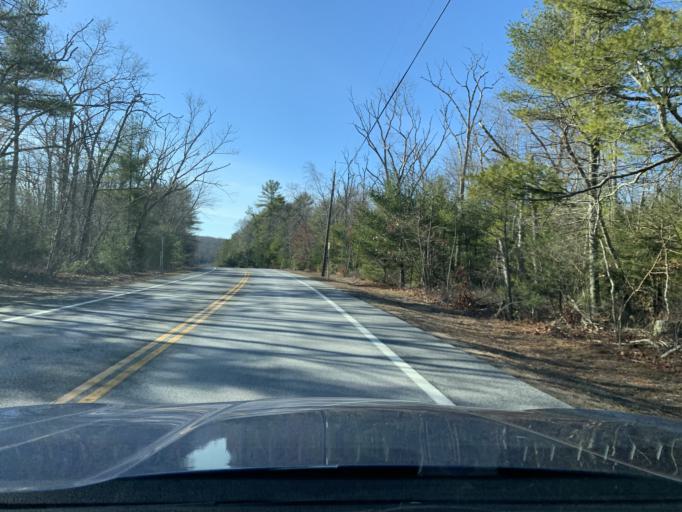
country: US
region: Rhode Island
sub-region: Washington County
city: Hope Valley
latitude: 41.5759
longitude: -71.7815
